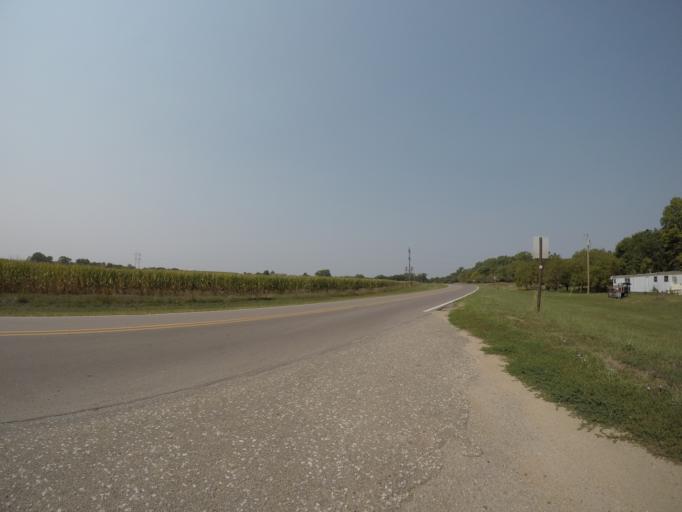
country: US
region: Nebraska
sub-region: Gage County
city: Beatrice
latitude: 40.2746
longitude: -96.7770
